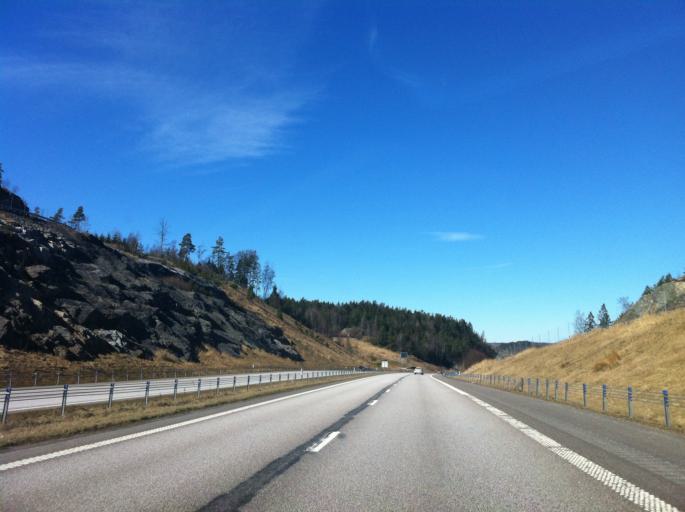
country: SE
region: Vaestra Goetaland
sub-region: Munkedals Kommun
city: Munkedal
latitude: 58.3725
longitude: 11.7880
